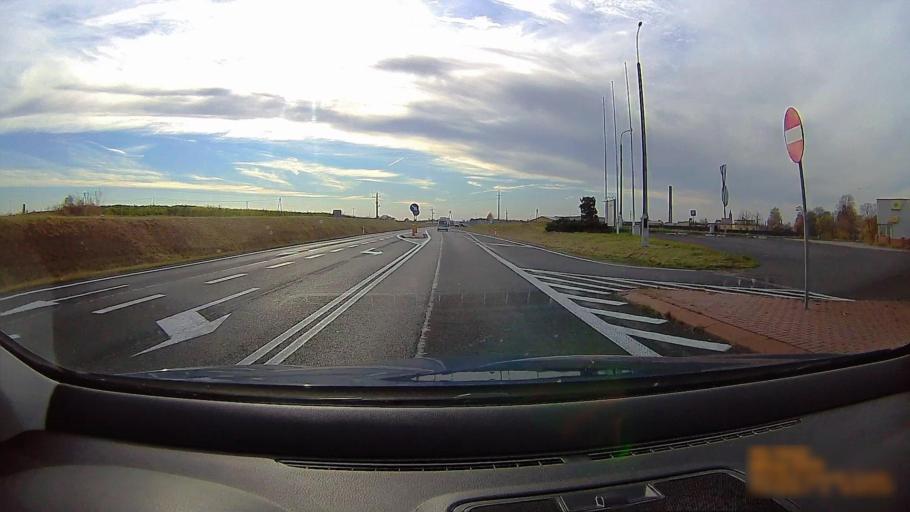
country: PL
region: Greater Poland Voivodeship
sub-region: Powiat kaliski
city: Stawiszyn
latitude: 51.9264
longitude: 18.1200
